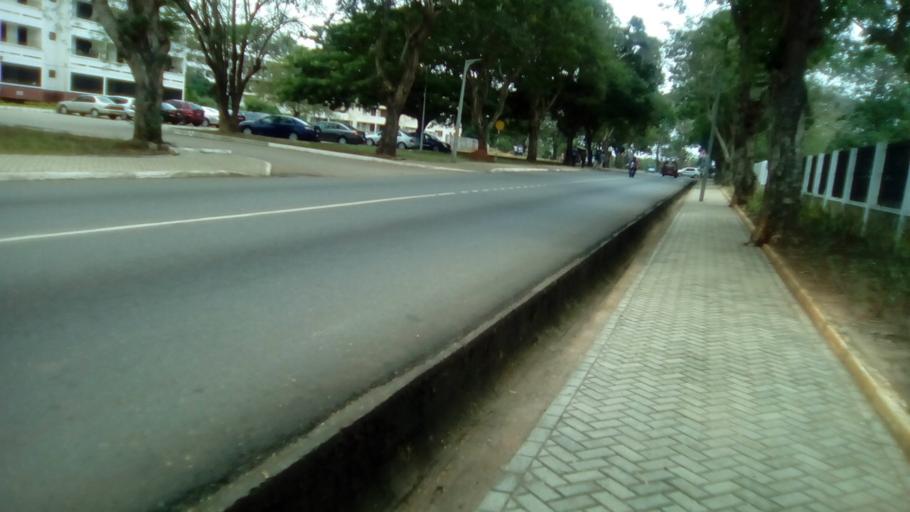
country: GH
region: Greater Accra
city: Medina Estates
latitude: 5.6437
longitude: -0.1871
